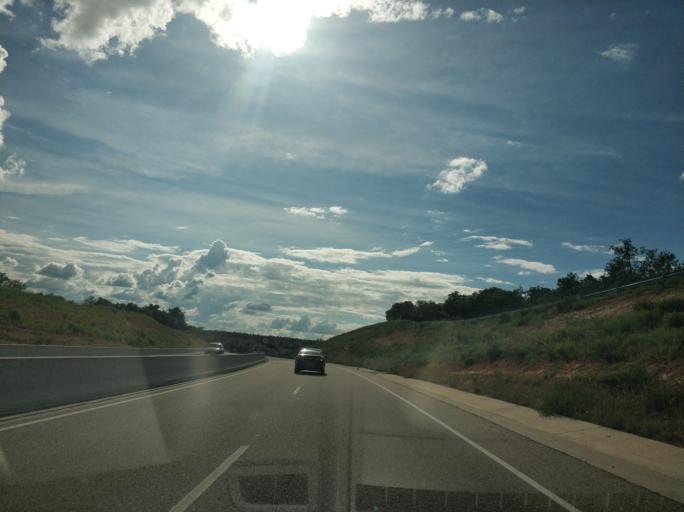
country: ES
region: Castille and Leon
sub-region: Provincia de Burgos
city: Aranda de Duero
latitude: 41.6991
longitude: -3.6794
